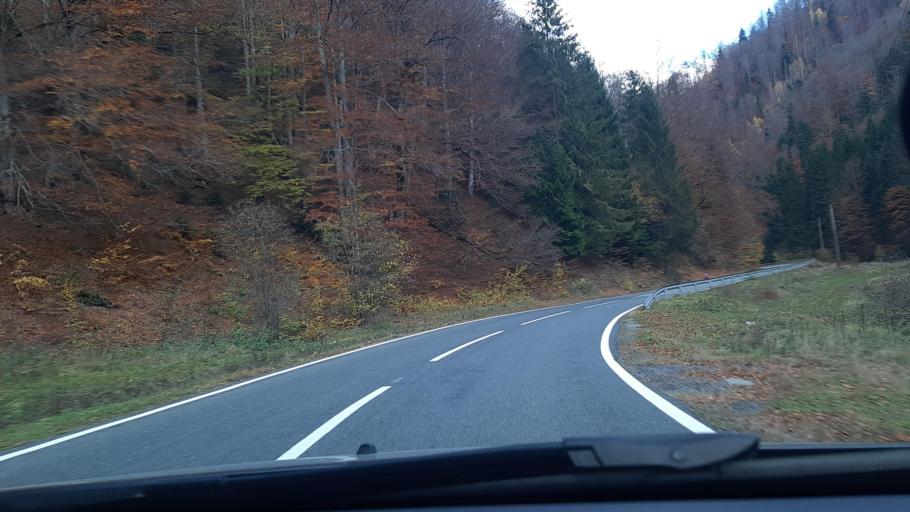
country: RO
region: Valcea
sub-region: Comuna Voineasa
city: Voineasa
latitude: 45.4251
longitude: 23.9232
